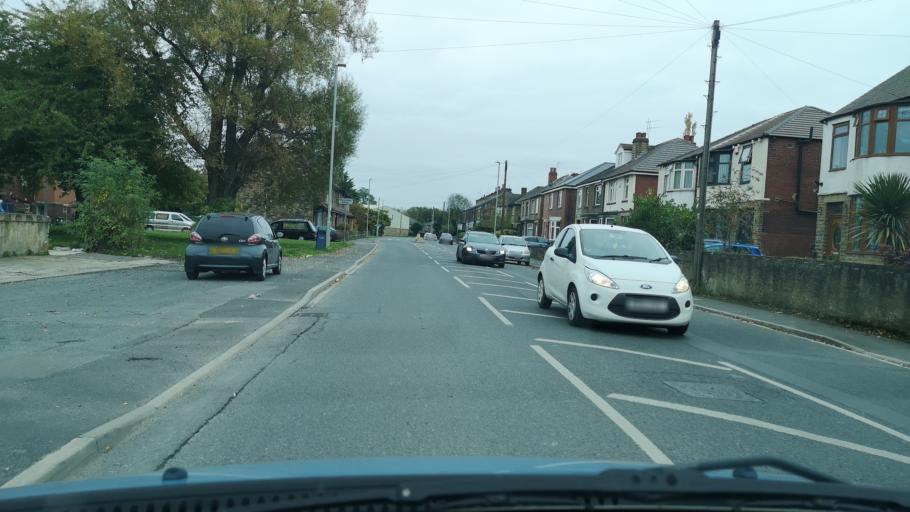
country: GB
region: England
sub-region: Kirklees
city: Dewsbury
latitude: 53.6739
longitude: -1.6491
